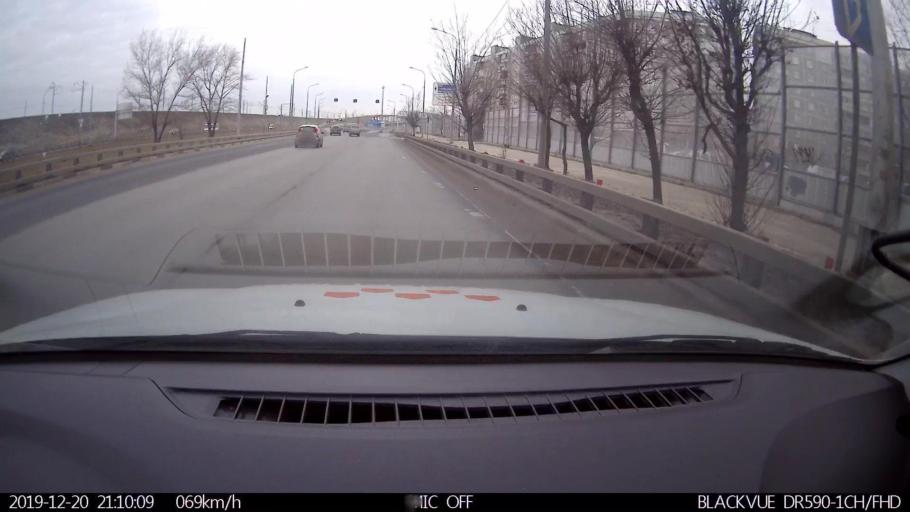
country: RU
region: Nizjnij Novgorod
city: Nizhniy Novgorod
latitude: 56.3424
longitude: 43.9226
